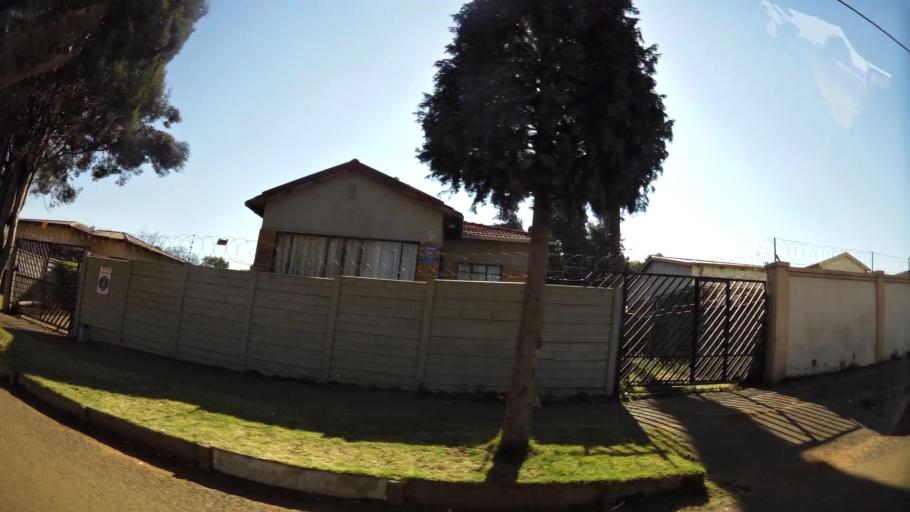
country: ZA
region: Gauteng
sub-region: City of Johannesburg Metropolitan Municipality
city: Johannesburg
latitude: -26.1952
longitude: 27.9806
